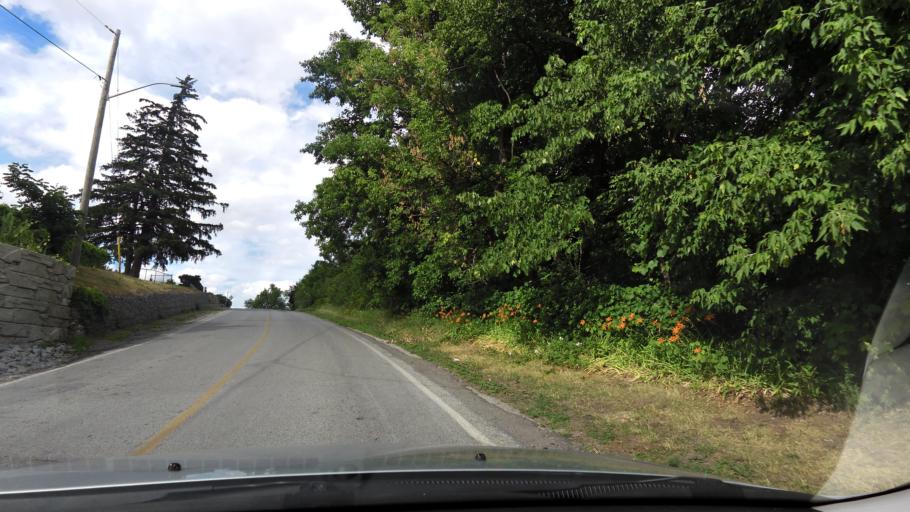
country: CA
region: Ontario
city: Brampton
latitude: 43.6724
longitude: -79.9222
